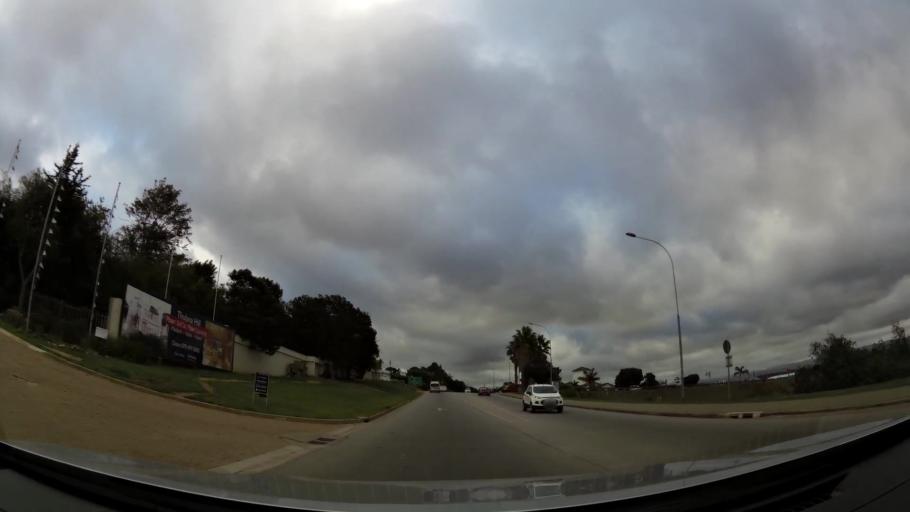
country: ZA
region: Western Cape
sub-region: Eden District Municipality
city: Plettenberg Bay
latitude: -34.0510
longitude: 23.3597
